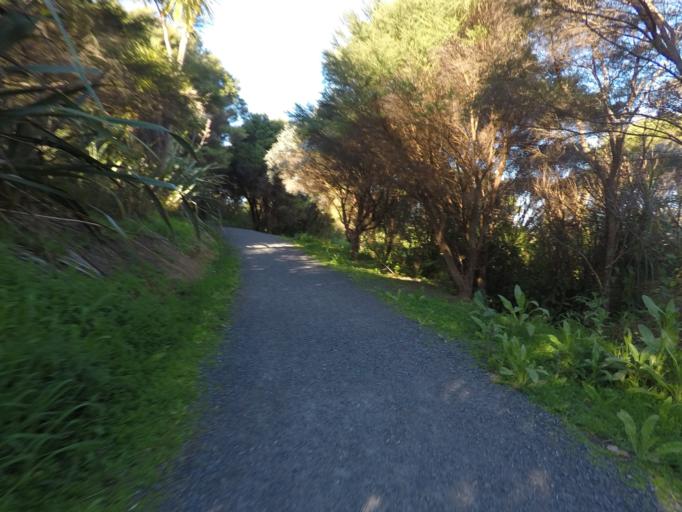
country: NZ
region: Auckland
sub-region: Auckland
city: Rosebank
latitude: -36.8493
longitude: 174.6537
